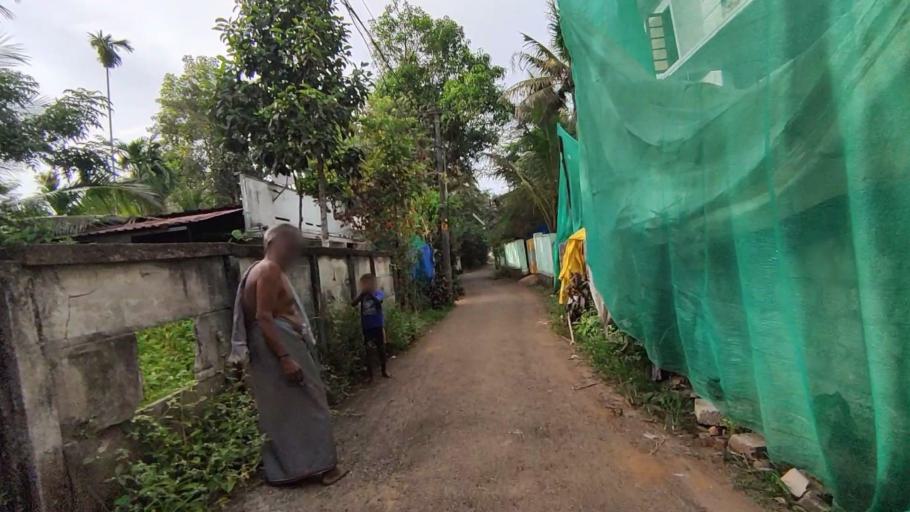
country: IN
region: Kerala
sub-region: Kottayam
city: Kottayam
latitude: 9.5702
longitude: 76.4899
